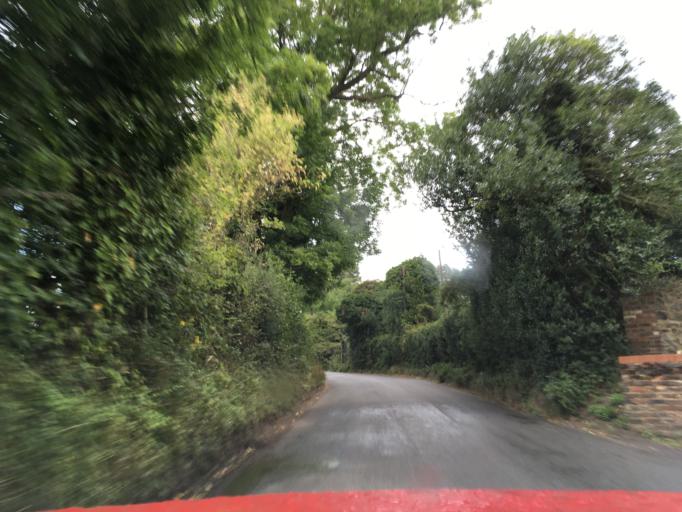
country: GB
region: England
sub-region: Kent
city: Yalding
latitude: 51.2227
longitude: 0.4759
